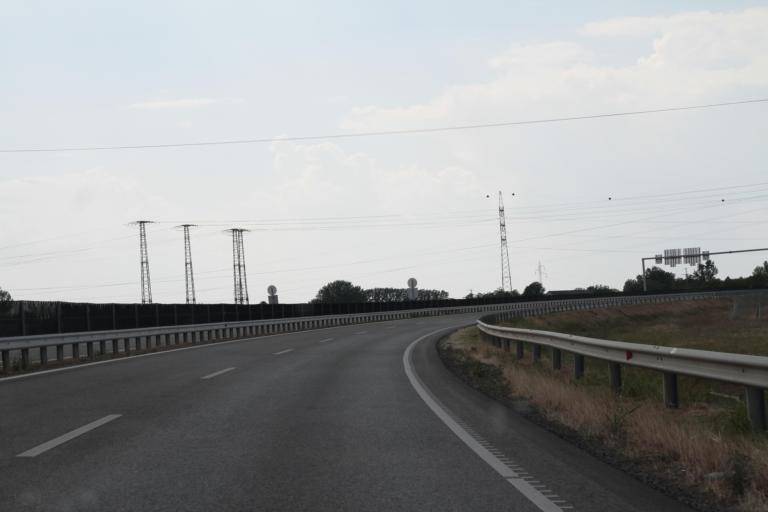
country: HU
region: Bekes
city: Bekescsaba
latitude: 46.6938
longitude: 21.0551
